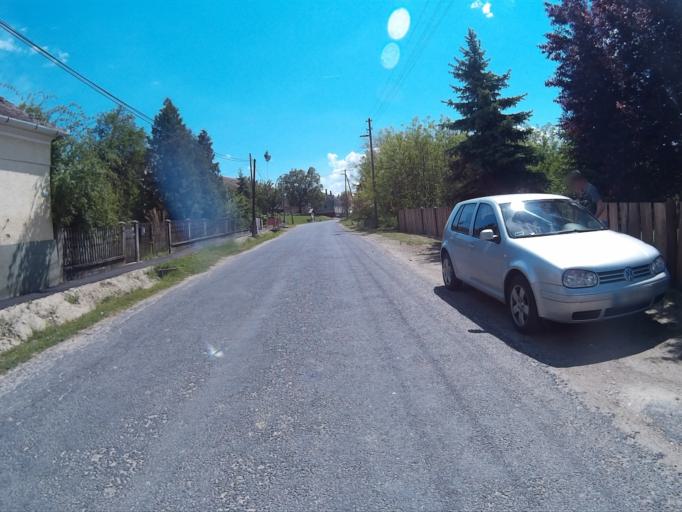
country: HU
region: Zala
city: Zalalovo
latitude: 46.9346
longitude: 16.5199
